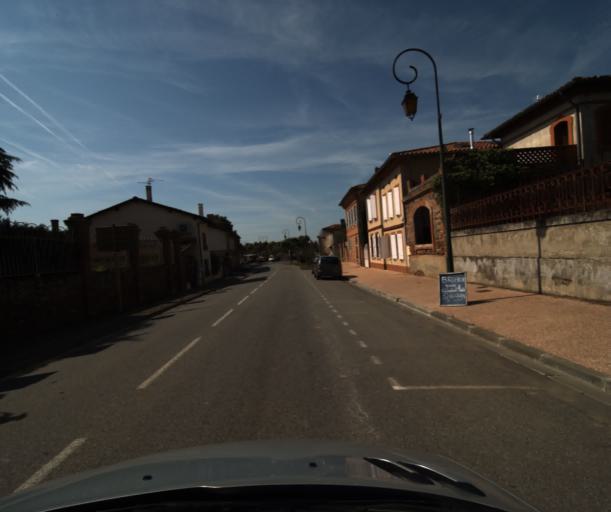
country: FR
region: Midi-Pyrenees
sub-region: Departement de la Haute-Garonne
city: Labastidette
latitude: 43.4673
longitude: 1.2162
